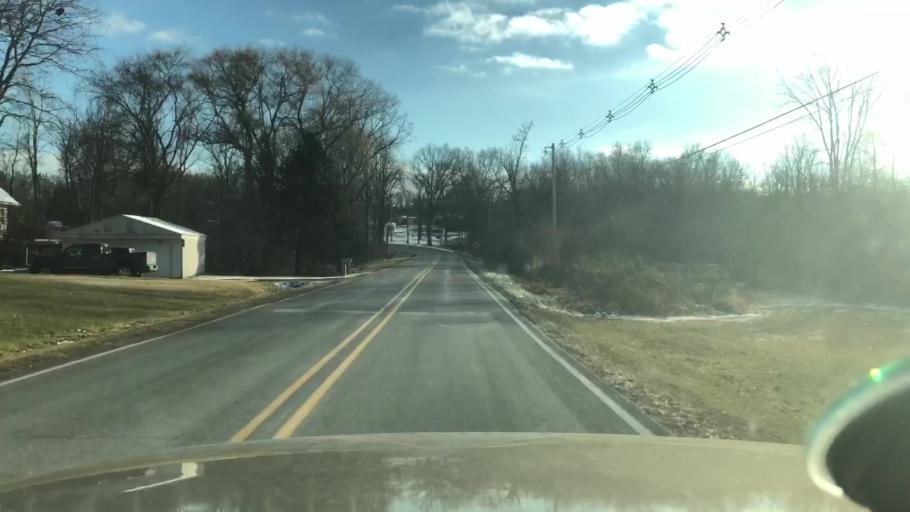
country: US
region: Michigan
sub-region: Jackson County
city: Vandercook Lake
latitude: 42.1627
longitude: -84.4526
